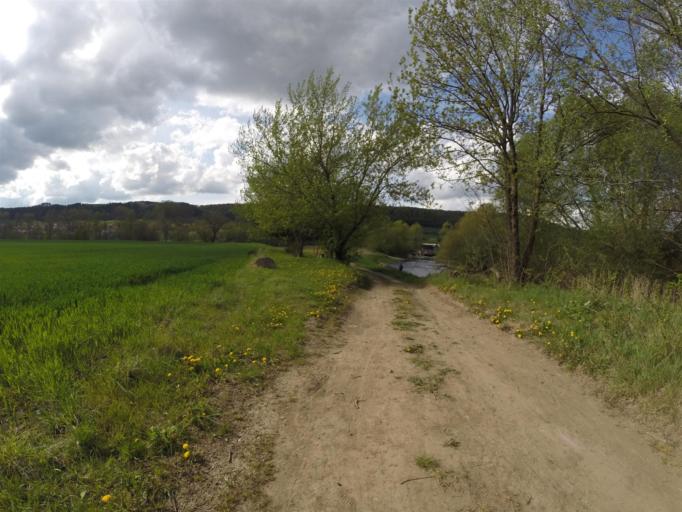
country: DE
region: Thuringia
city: Neuengonna
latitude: 50.9666
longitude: 11.6387
